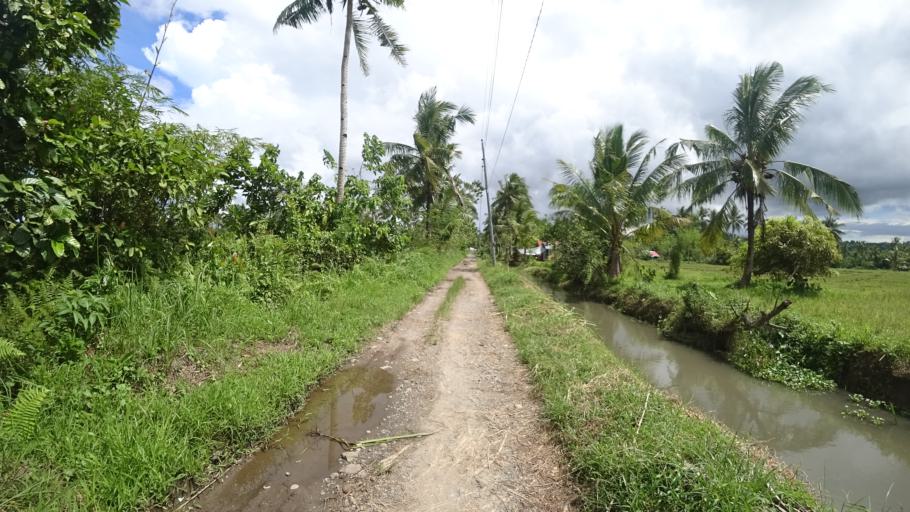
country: PH
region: Eastern Visayas
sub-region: Province of Leyte
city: MacArthur
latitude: 10.8487
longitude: 124.9650
